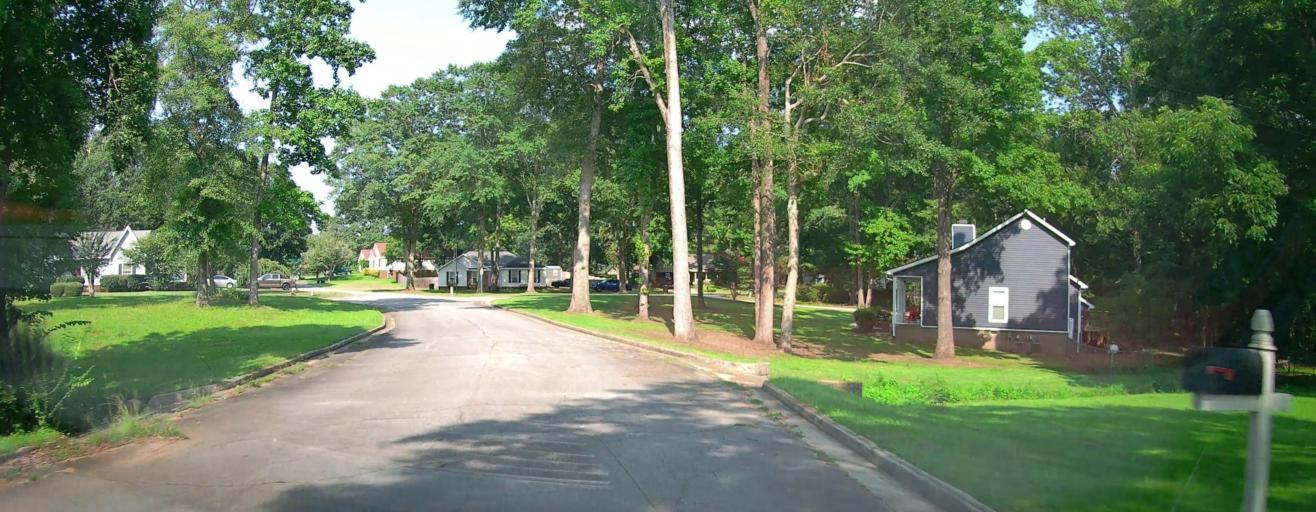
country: US
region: Georgia
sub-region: Houston County
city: Centerville
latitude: 32.6437
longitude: -83.6941
